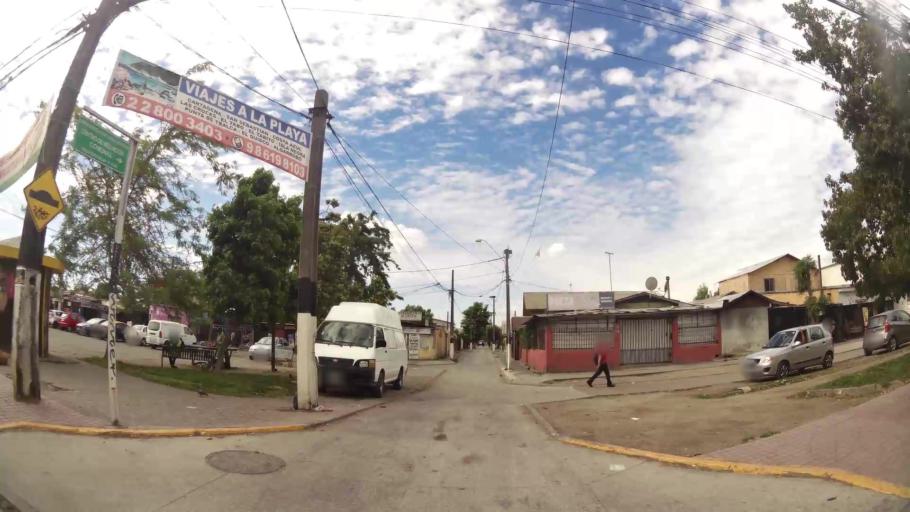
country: CL
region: Santiago Metropolitan
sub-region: Provincia de Santiago
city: La Pintana
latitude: -33.5825
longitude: -70.6338
